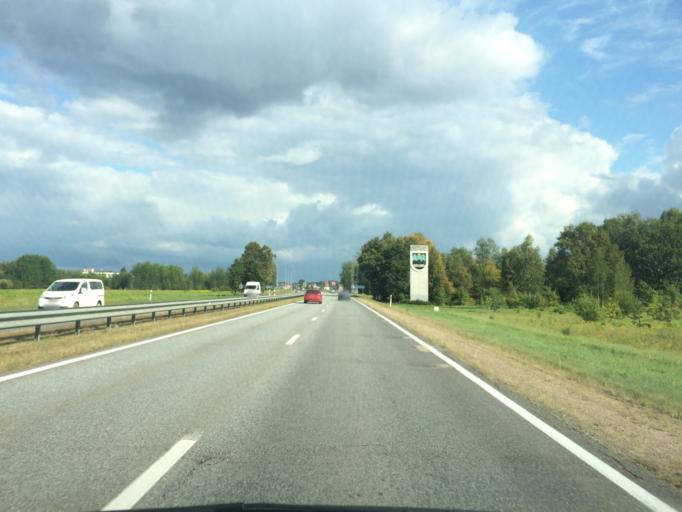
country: LV
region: Ikskile
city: Ikskile
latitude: 56.8191
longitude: 24.5532
